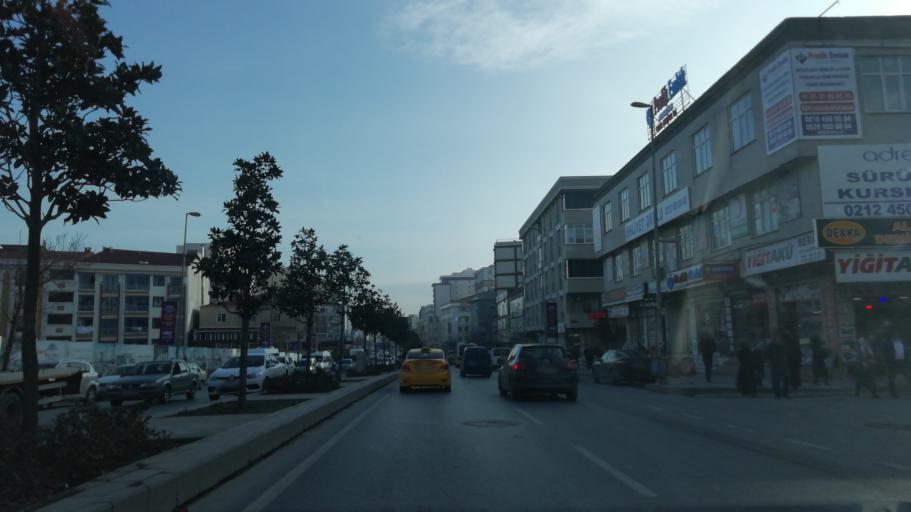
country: TR
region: Istanbul
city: Esenyurt
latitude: 41.0442
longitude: 28.6753
